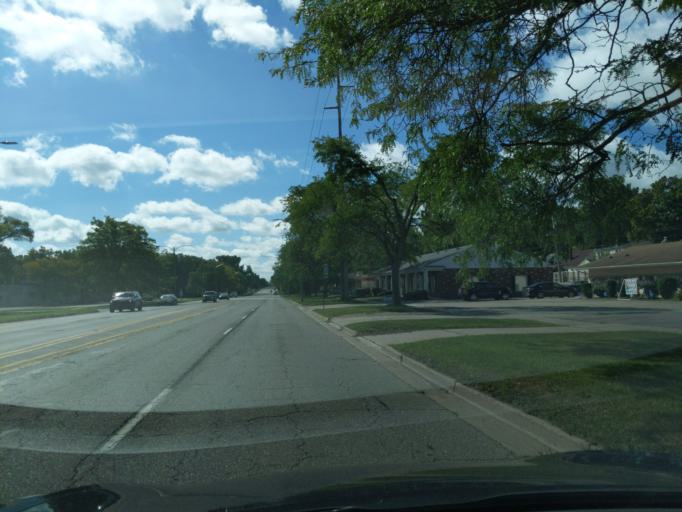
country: US
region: Michigan
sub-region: Ingham County
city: Lansing
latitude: 42.7002
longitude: -84.5382
